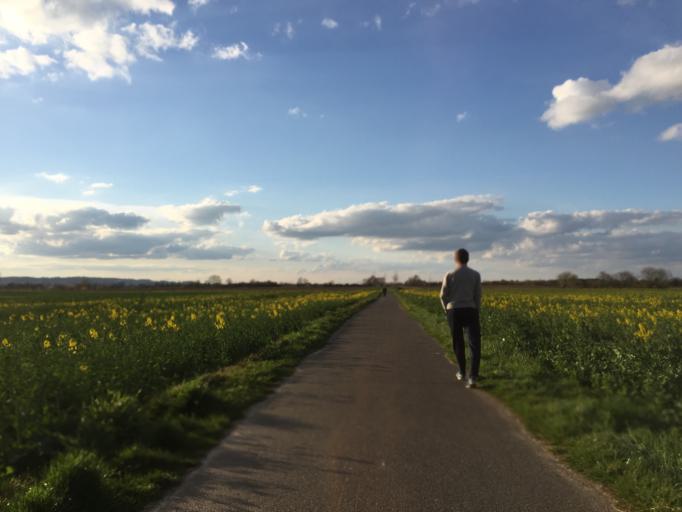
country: DE
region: North Rhine-Westphalia
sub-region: Regierungsbezirk Koln
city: Bonn
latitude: 50.7229
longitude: 7.0619
